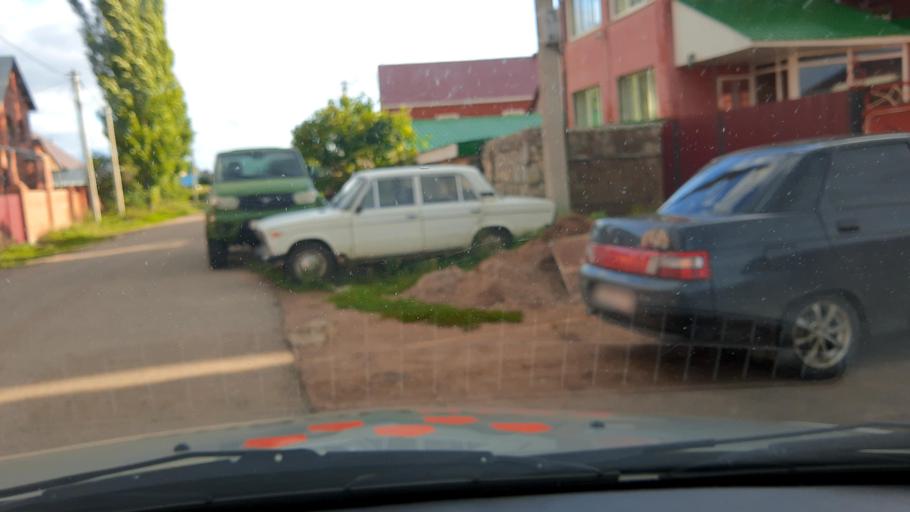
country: RU
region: Bashkortostan
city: Ufa
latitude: 54.8415
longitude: 56.0064
